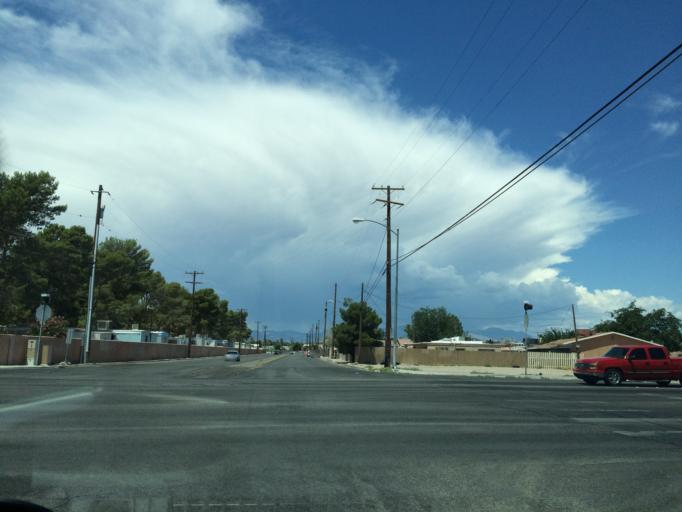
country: US
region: Nevada
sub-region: Clark County
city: Winchester
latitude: 36.1556
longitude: -115.1009
